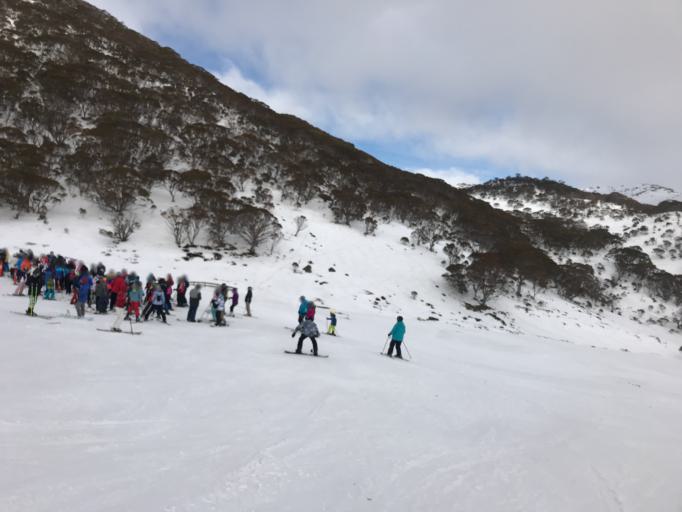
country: AU
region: New South Wales
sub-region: Snowy River
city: Jindabyne
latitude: -36.3851
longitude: 148.3782
